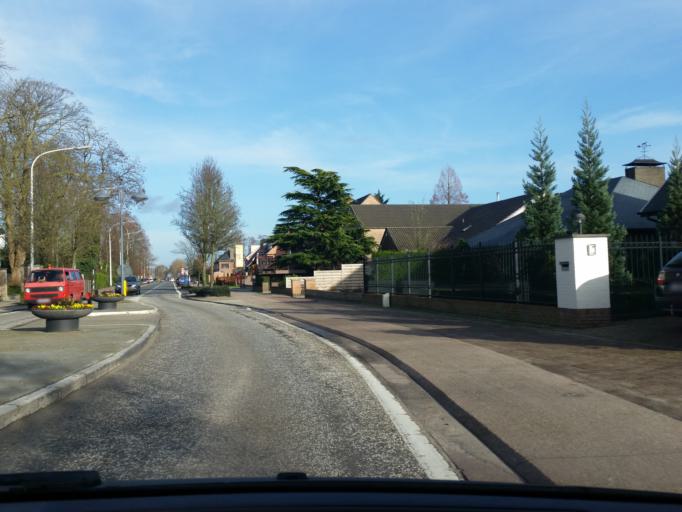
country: BE
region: Flanders
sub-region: Provincie Antwerpen
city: Wuustwezel
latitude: 51.3947
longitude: 4.5975
